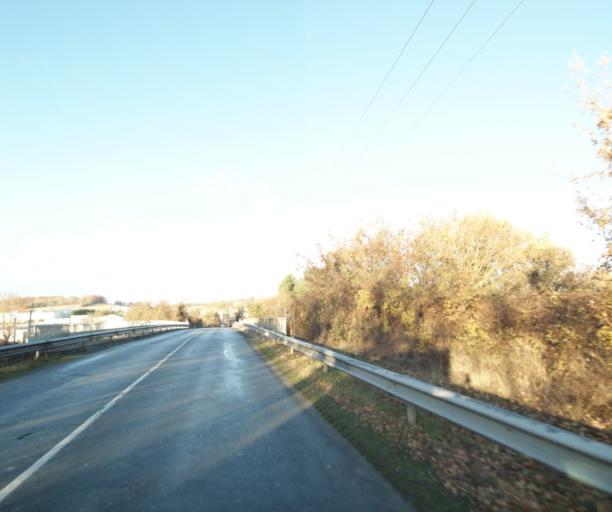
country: FR
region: Poitou-Charentes
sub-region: Departement de la Charente-Maritime
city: Saintes
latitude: 45.7505
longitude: -0.6709
